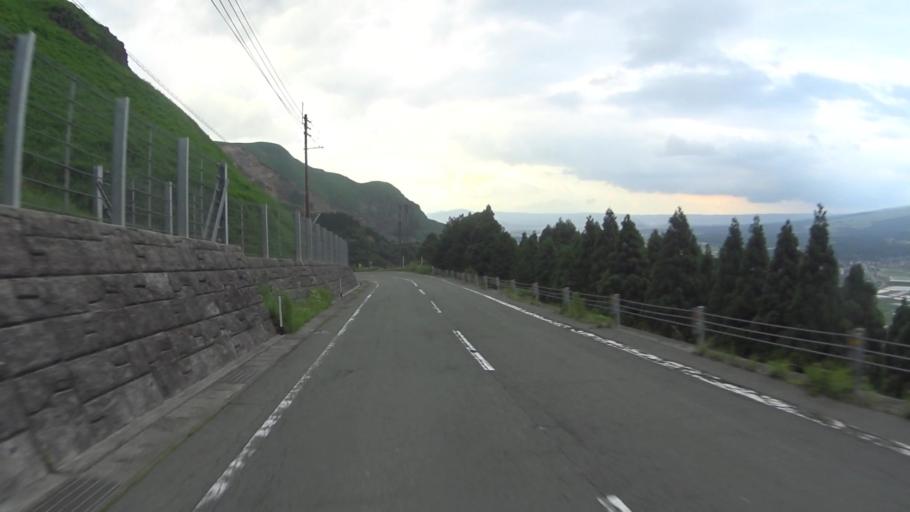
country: JP
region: Kumamoto
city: Ozu
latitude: 32.9142
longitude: 130.9690
